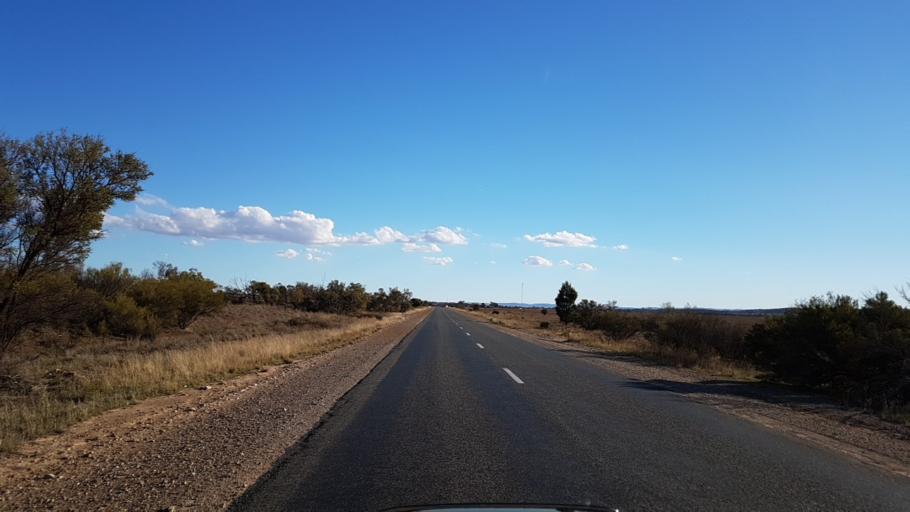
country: AU
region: South Australia
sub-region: Peterborough
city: Peterborough
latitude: -32.9632
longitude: 138.8836
